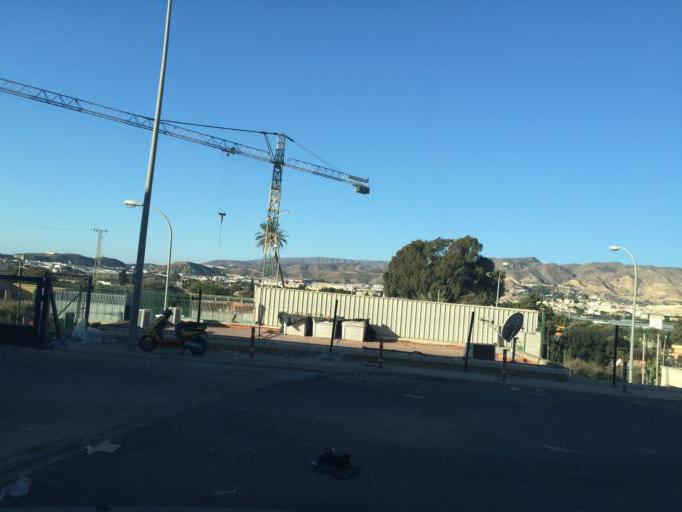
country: ES
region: Andalusia
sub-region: Provincia de Almeria
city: Viator
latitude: 36.8781
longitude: -2.4227
